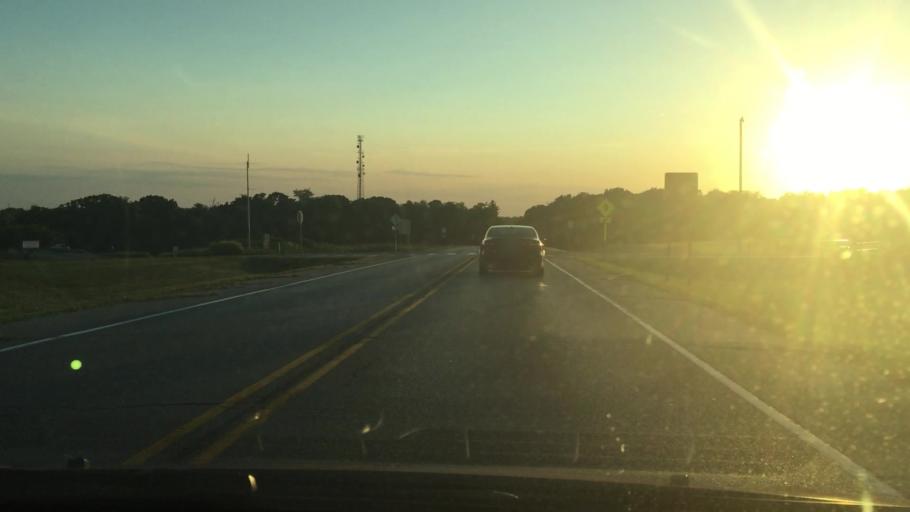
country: US
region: Iowa
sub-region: Muscatine County
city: Muscatine
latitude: 41.4361
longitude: -91.0831
